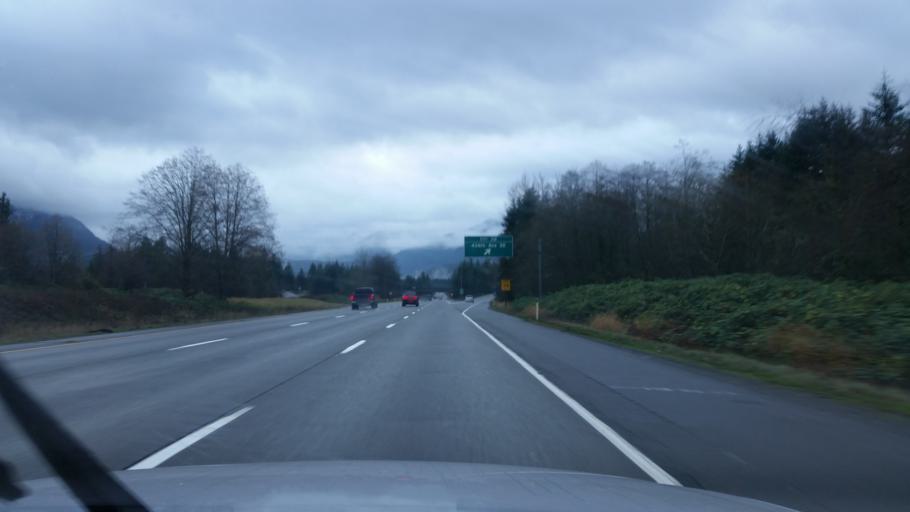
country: US
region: Washington
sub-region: King County
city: Riverbend
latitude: 47.4732
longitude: -121.7662
